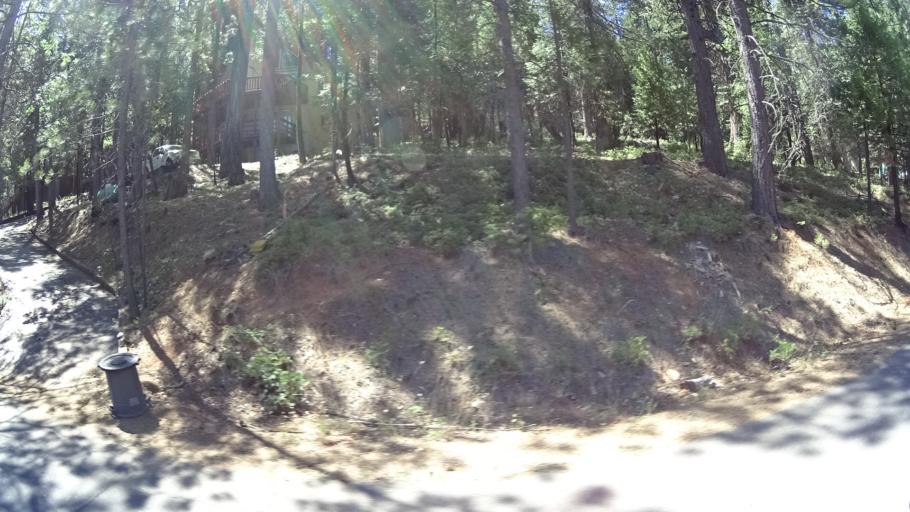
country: US
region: California
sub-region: Calaveras County
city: Arnold
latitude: 38.2322
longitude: -120.3403
